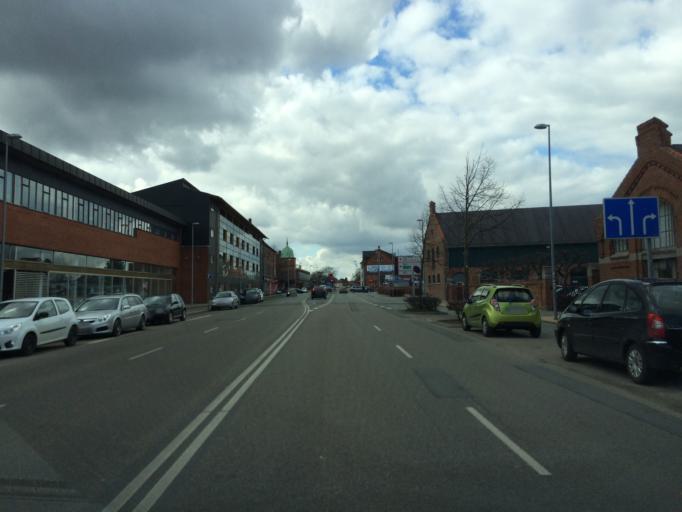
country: DK
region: South Denmark
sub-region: Odense Kommune
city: Odense
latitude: 55.3990
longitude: 10.3701
